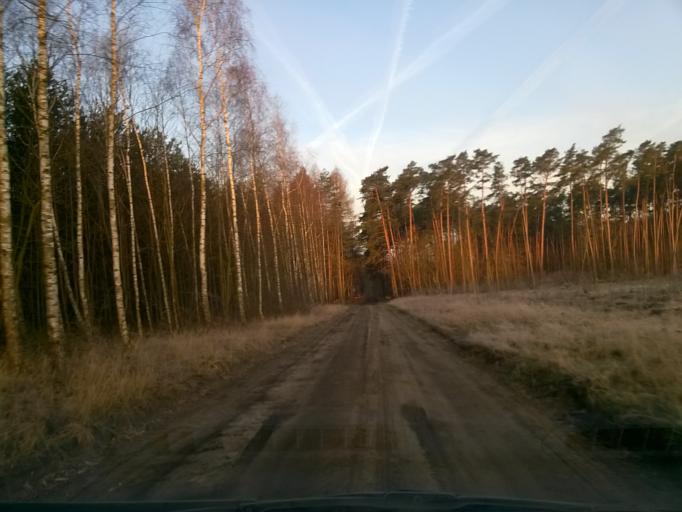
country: PL
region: Kujawsko-Pomorskie
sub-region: Powiat nakielski
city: Sadki
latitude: 53.1218
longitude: 17.4202
